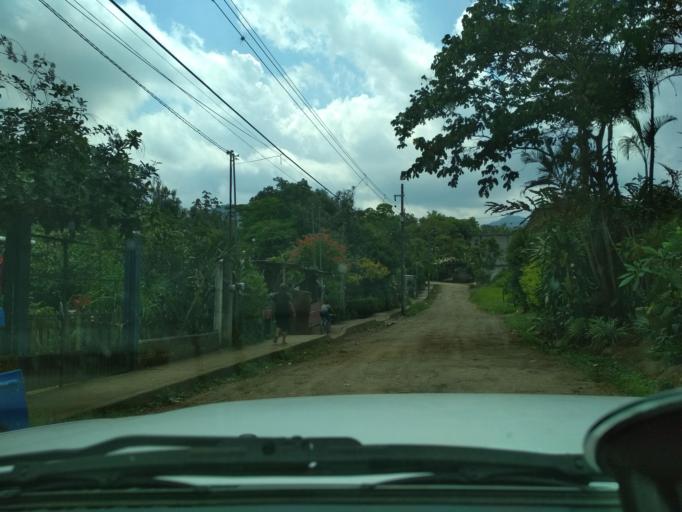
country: MX
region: Veracruz
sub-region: Fortin
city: Monte Salas
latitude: 18.9377
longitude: -97.0138
